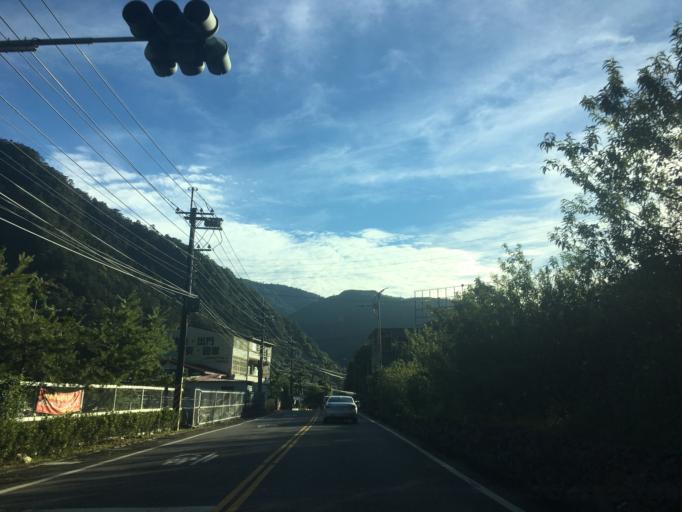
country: TW
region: Taiwan
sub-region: Nantou
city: Puli
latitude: 23.9997
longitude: 121.0805
